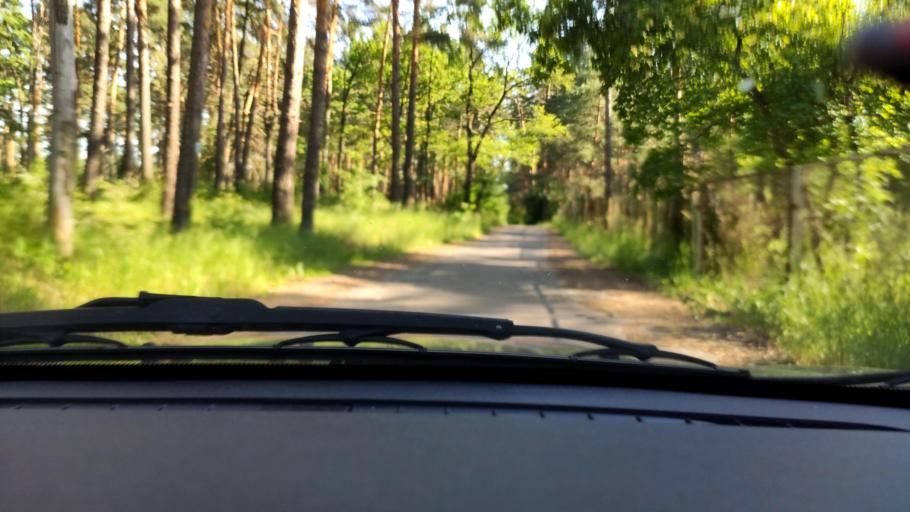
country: RU
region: Voronezj
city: Somovo
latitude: 51.7576
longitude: 39.3746
